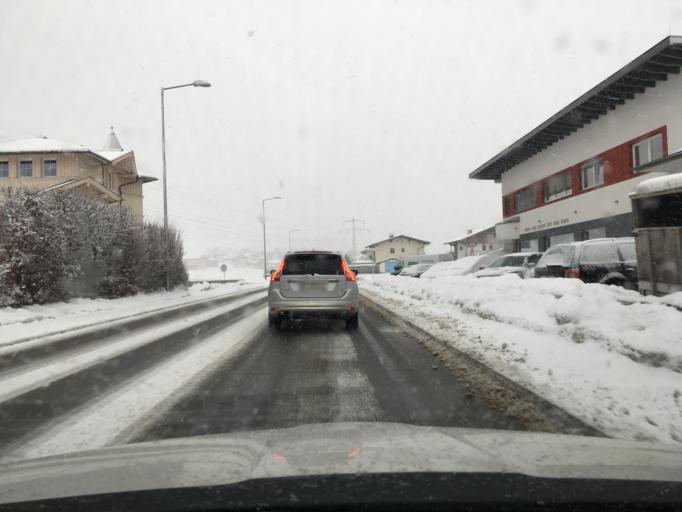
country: AT
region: Tyrol
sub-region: Politischer Bezirk Schwaz
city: Ramsau im Zillertal
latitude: 47.2011
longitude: 11.8715
